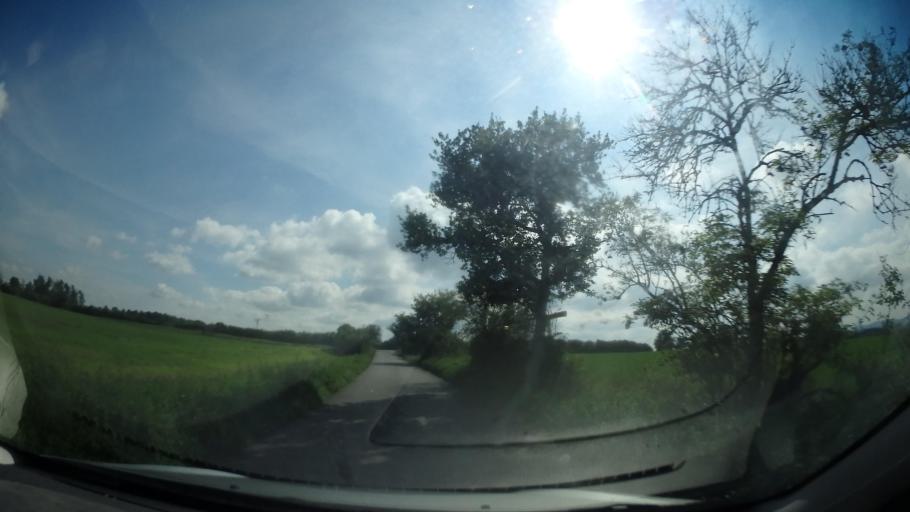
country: CZ
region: Central Bohemia
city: Krasna Hora nad Vltavou
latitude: 49.6814
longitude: 14.3211
